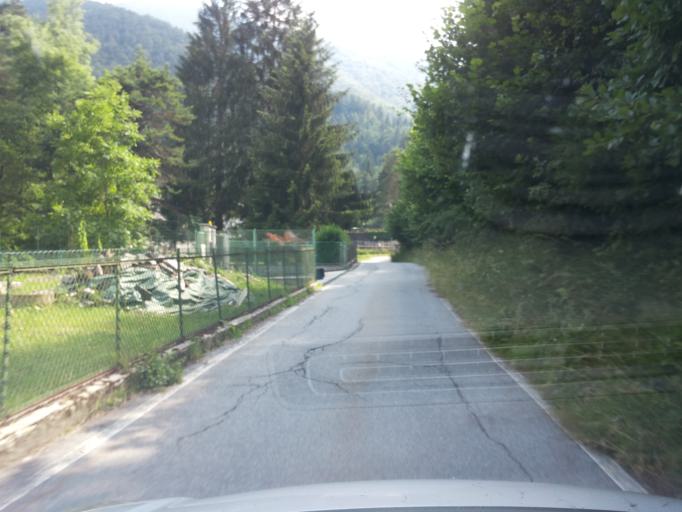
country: IT
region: Piedmont
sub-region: Provincia Verbano-Cusio-Ossola
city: Malesco
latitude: 46.1273
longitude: 8.4945
